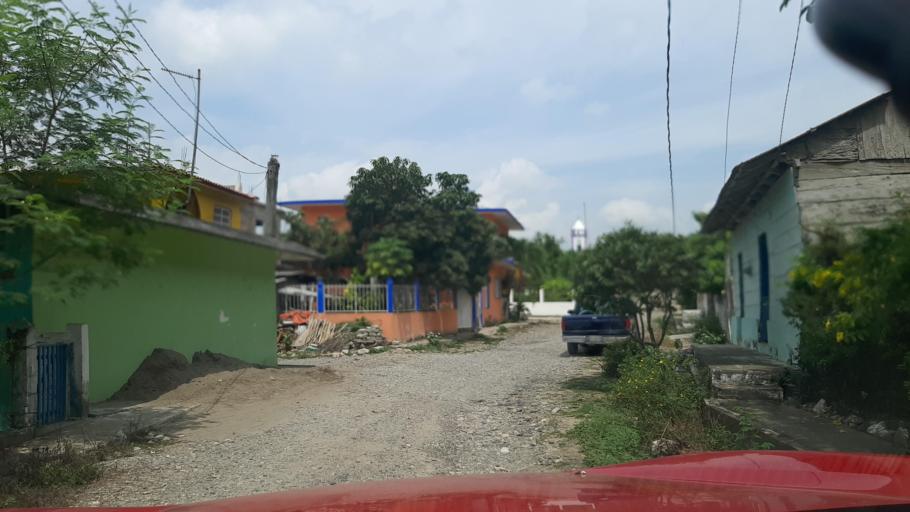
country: MX
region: Veracruz
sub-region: Papantla
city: Polutla
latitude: 20.4632
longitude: -97.1882
